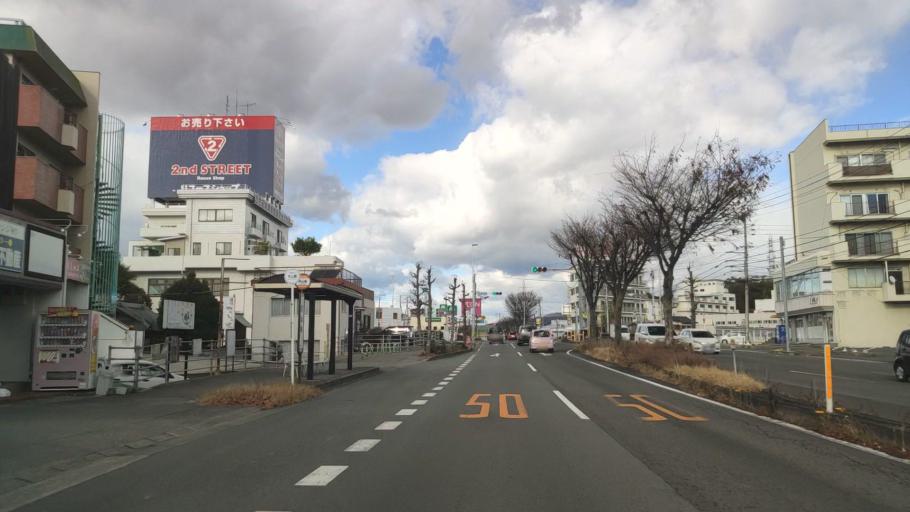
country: JP
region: Ehime
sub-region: Shikoku-chuo Shi
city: Matsuyama
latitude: 33.8169
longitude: 132.7770
